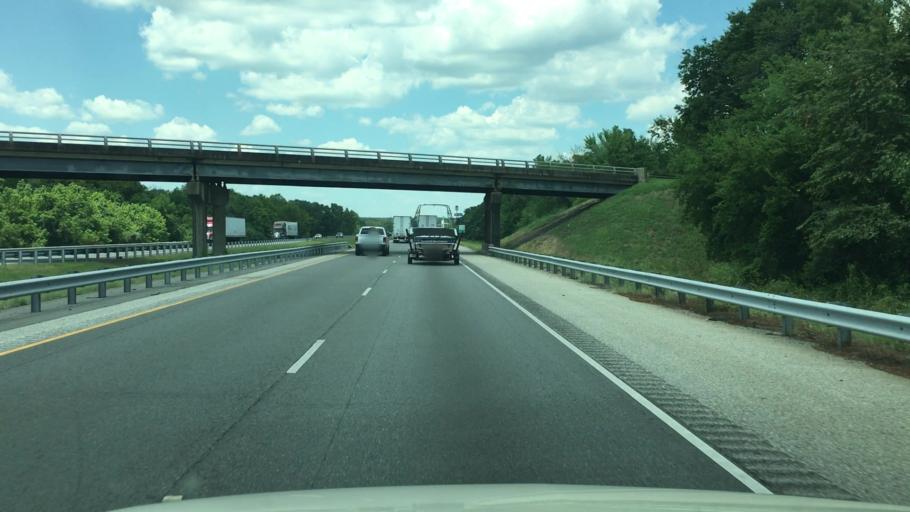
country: US
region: Arkansas
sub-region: Clark County
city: Arkadelphia
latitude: 34.1715
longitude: -93.0748
